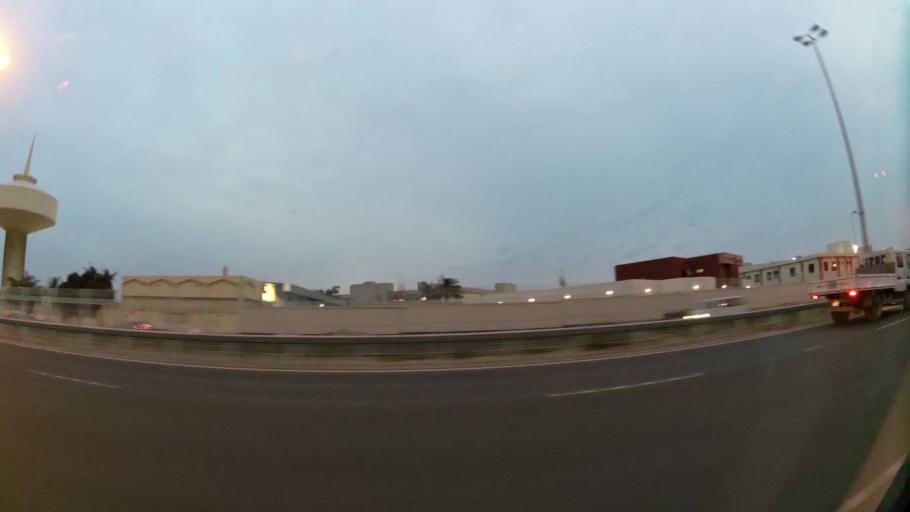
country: BH
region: Northern
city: Madinat `Isa
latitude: 26.1672
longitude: 50.5475
